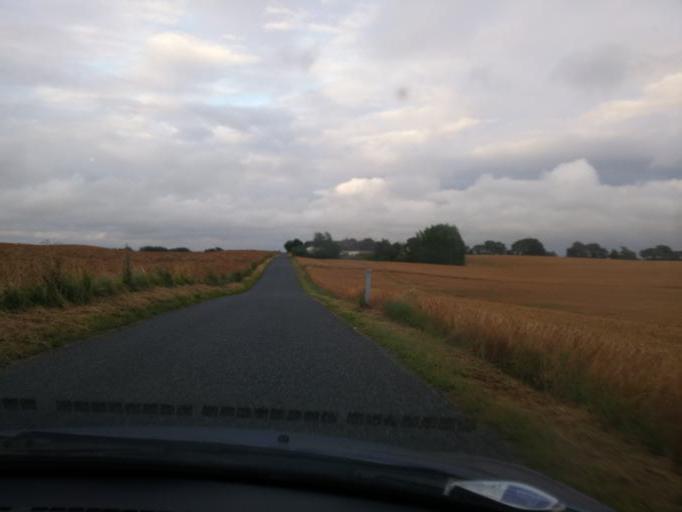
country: DK
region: South Denmark
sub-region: Kerteminde Kommune
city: Munkebo
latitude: 55.5212
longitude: 10.5783
